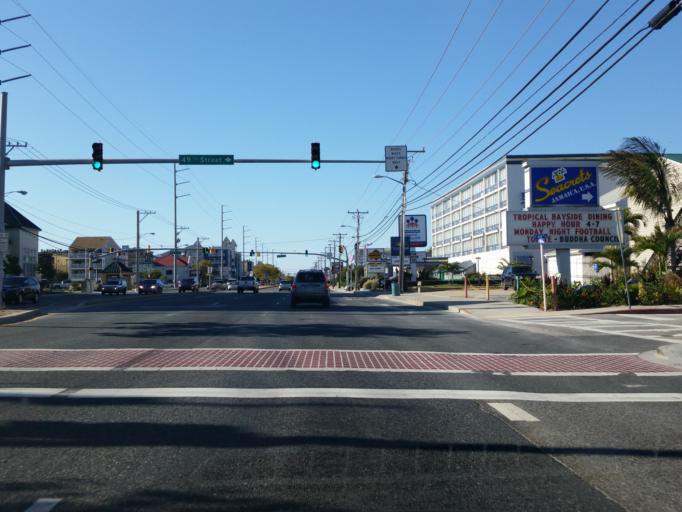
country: US
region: Maryland
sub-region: Worcester County
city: Ocean City
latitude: 38.3746
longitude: -75.0697
